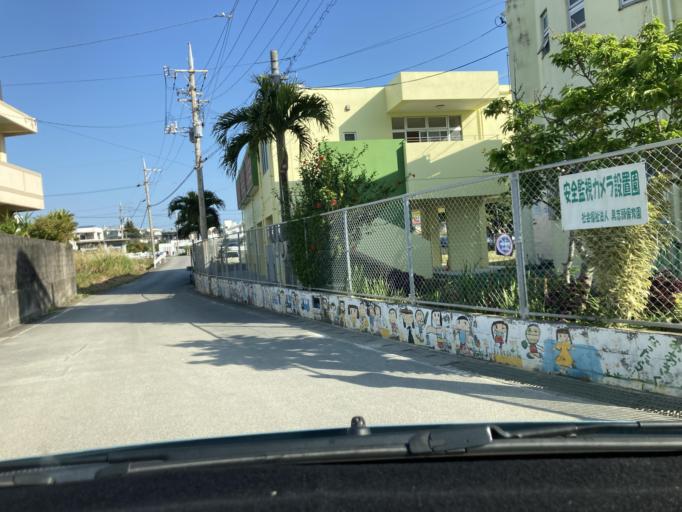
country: JP
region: Okinawa
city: Itoman
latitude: 26.1211
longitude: 127.7465
